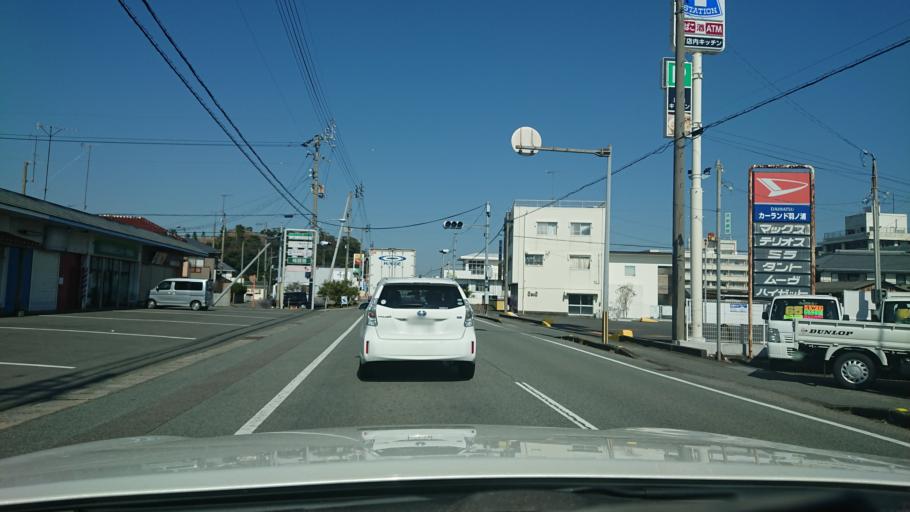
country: JP
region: Tokushima
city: Anan
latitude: 33.9531
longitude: 134.6264
